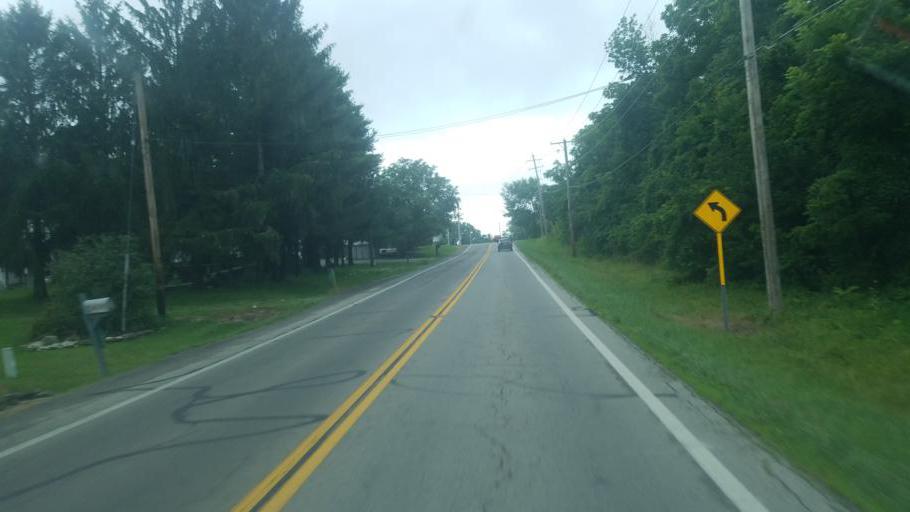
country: US
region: Ohio
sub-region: Logan County
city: Russells Point
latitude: 40.5282
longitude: -83.8525
